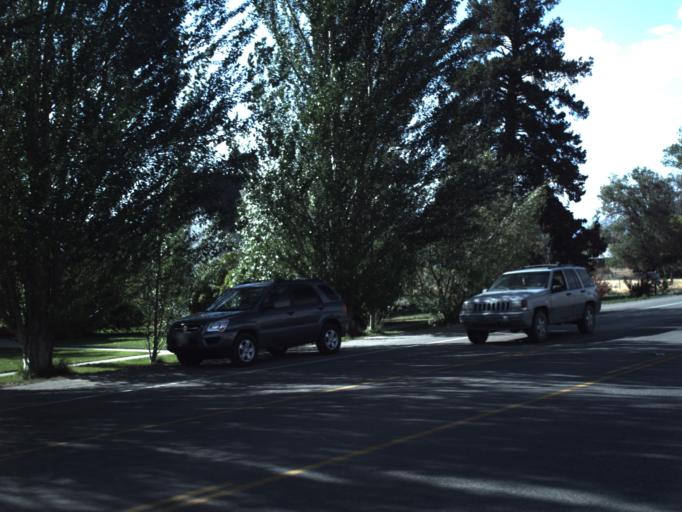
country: US
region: Utah
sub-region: Sanpete County
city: Ephraim
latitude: 39.3660
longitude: -111.5870
